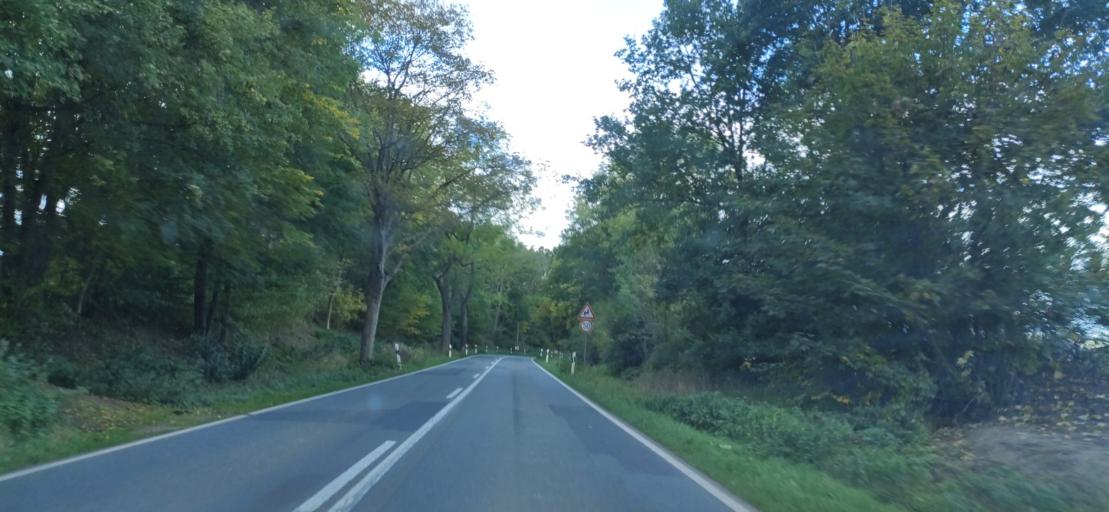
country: DE
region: Mecklenburg-Vorpommern
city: Grabowhofe
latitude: 53.6470
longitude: 12.5398
